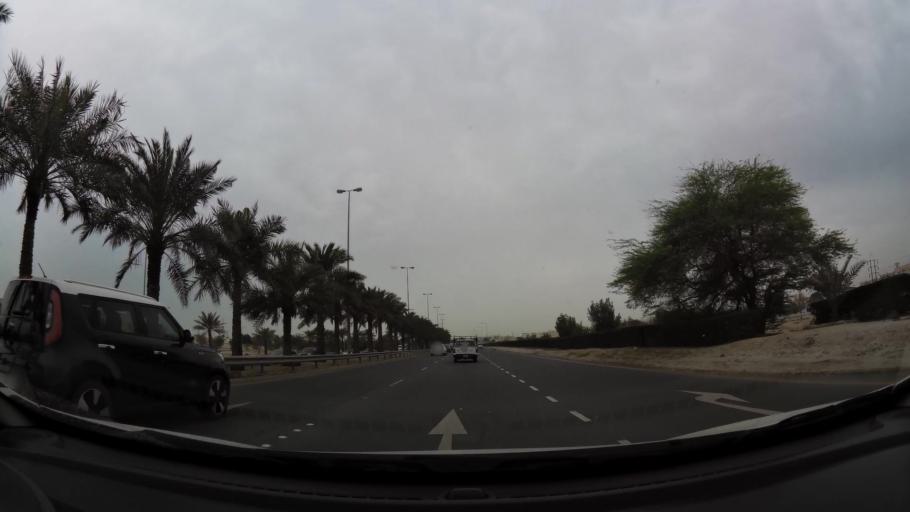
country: BH
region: Northern
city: Madinat `Isa
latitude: 26.1539
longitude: 50.5366
